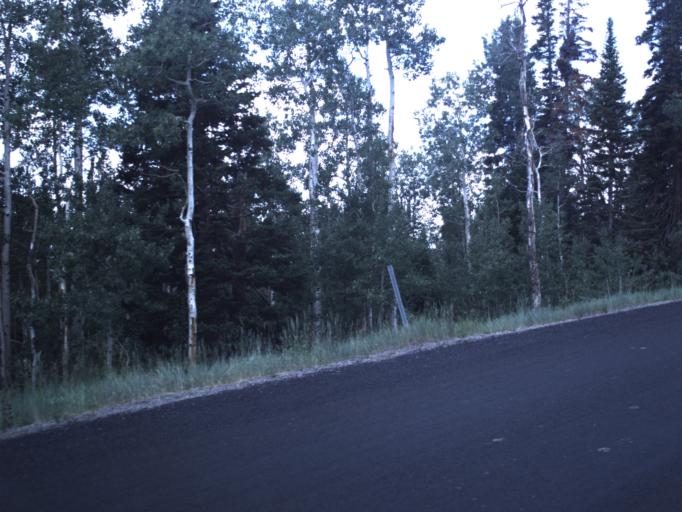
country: US
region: Utah
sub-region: Summit County
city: Francis
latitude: 40.4954
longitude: -111.0367
